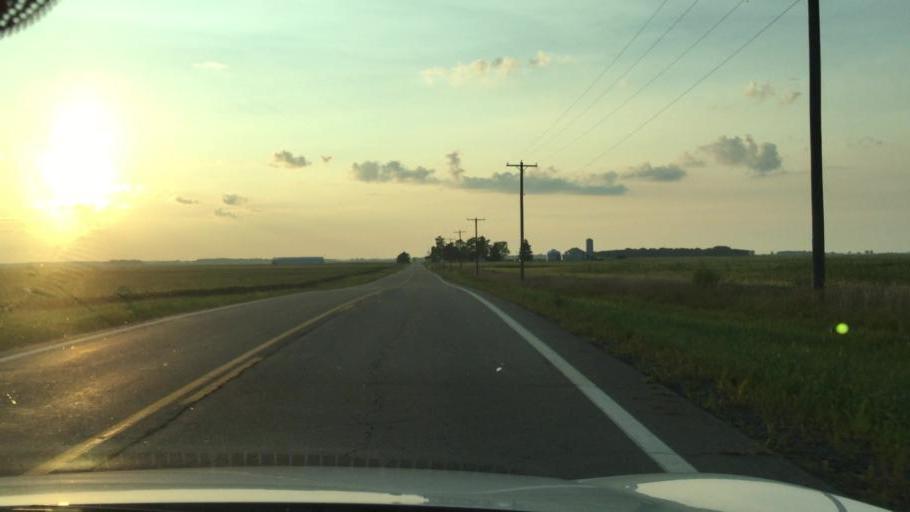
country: US
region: Ohio
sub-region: Madison County
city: Choctaw Lake
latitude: 39.9987
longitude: -83.4301
